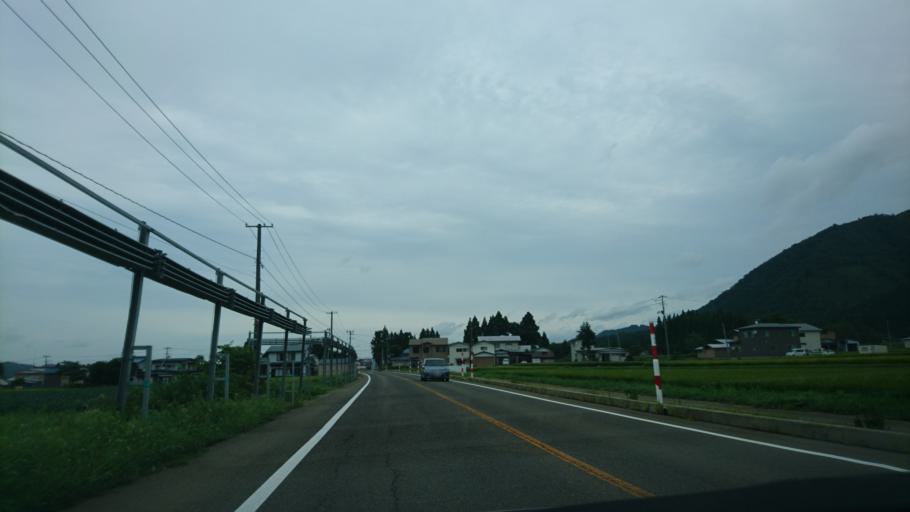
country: JP
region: Akita
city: Yuzawa
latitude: 39.1246
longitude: 140.5771
